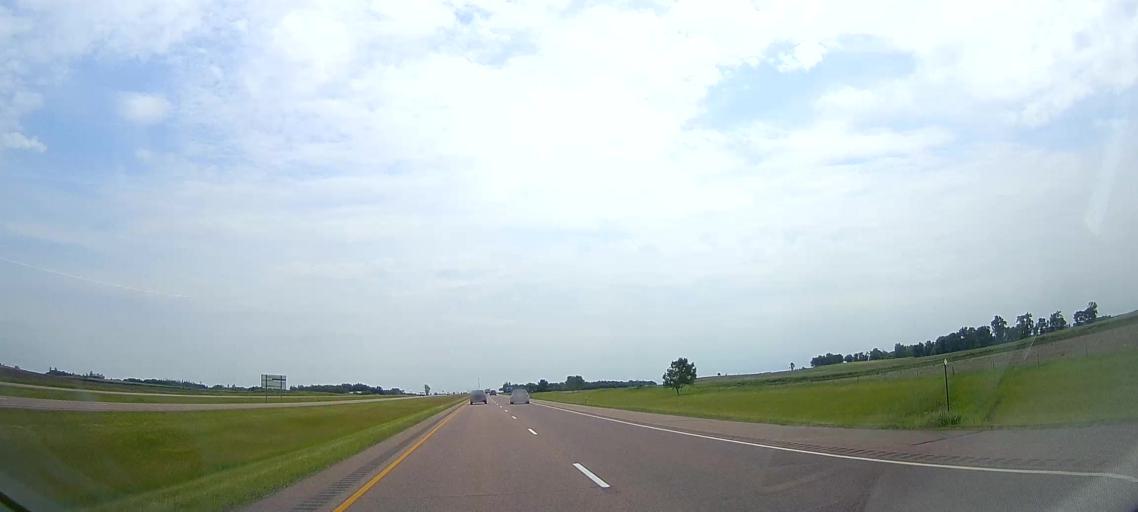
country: US
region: South Dakota
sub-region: Minnehaha County
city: Hartford
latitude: 43.6534
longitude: -97.1022
